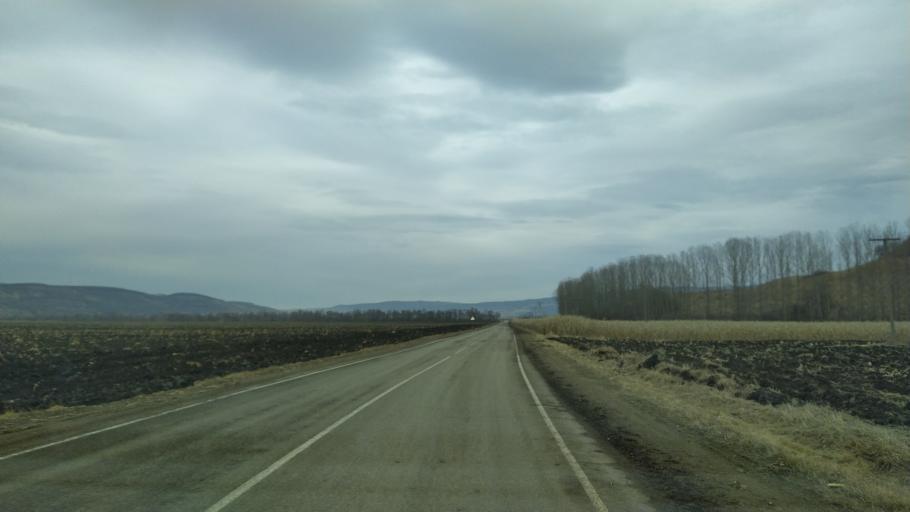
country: RU
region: Krasnodarskiy
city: Peredovaya
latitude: 44.1049
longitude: 41.4176
